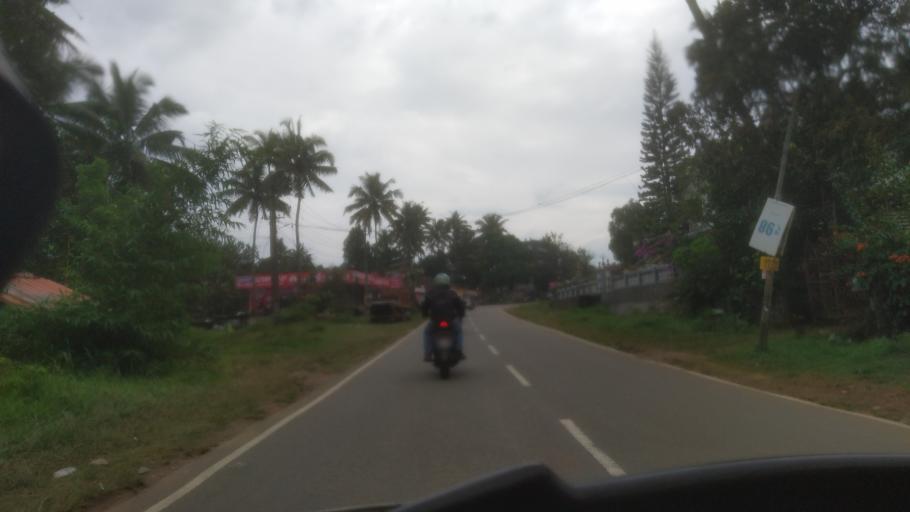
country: IN
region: Kerala
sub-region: Idukki
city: Munnar
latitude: 9.9957
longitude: 76.9756
